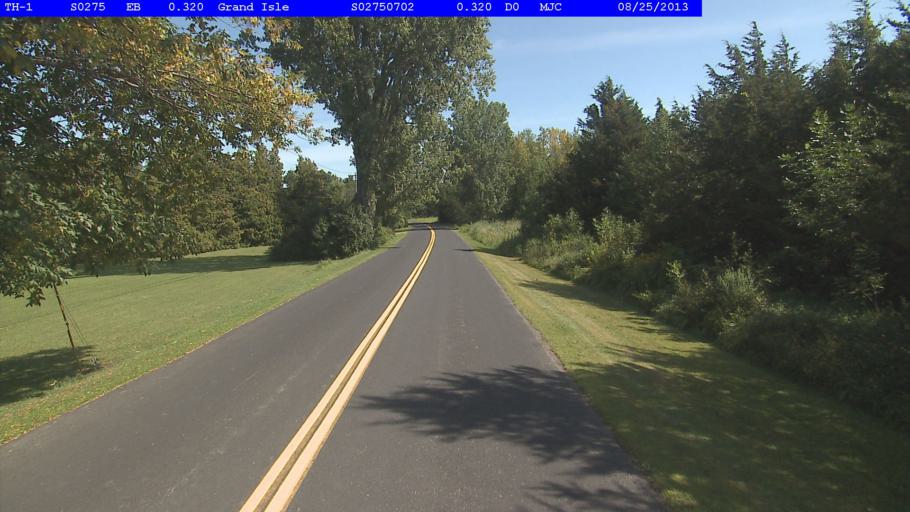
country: US
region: New York
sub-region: Clinton County
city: Cumberland Head
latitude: 44.7055
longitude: -73.3453
